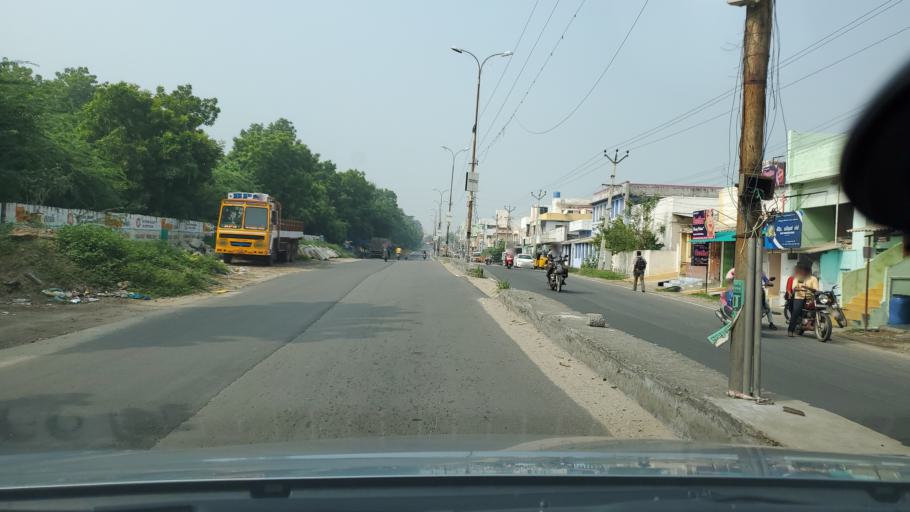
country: IN
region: Tamil Nadu
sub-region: Erode
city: Erode
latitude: 11.3274
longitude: 77.7210
